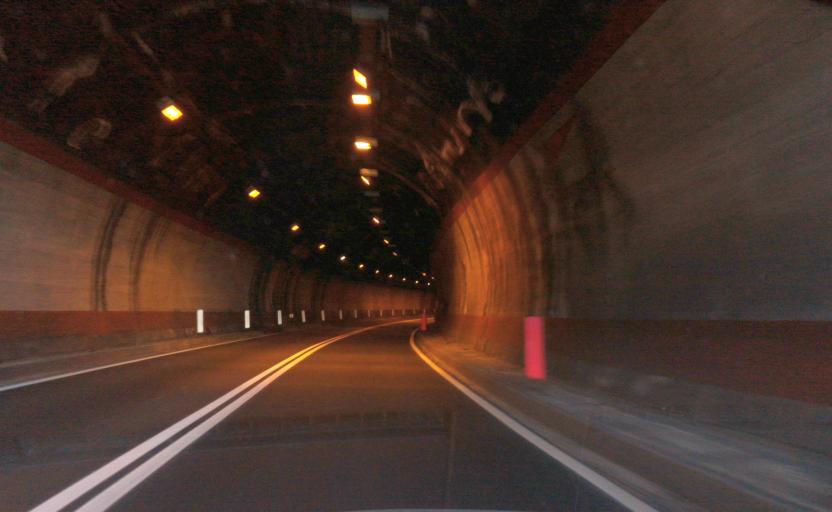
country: IT
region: Calabria
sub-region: Provincia di Cosenza
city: Zumpano
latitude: 39.2965
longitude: 16.2813
